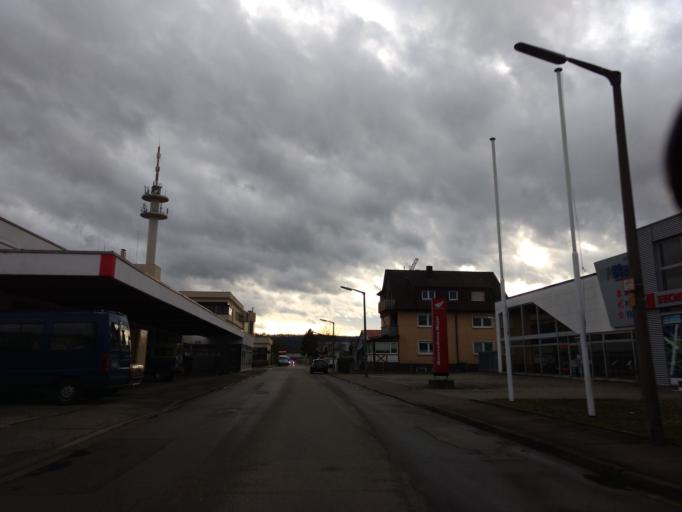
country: DE
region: Baden-Wuerttemberg
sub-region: Regierungsbezirk Stuttgart
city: Schorndorf
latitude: 48.8083
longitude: 9.5139
